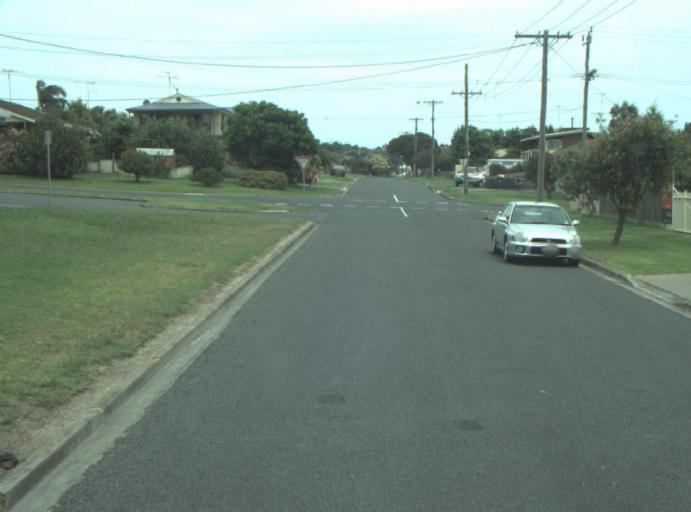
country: AU
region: Victoria
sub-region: Greater Geelong
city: Clifton Springs
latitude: -38.1483
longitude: 144.5745
